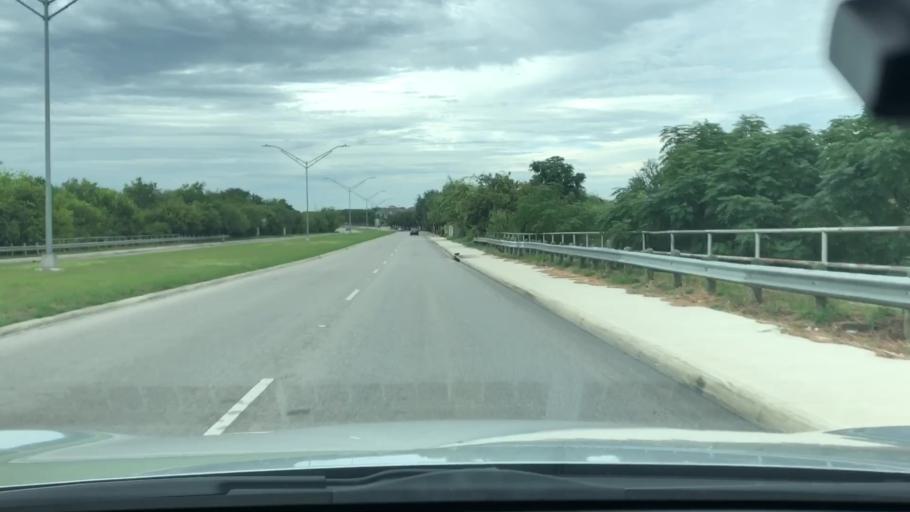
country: US
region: Texas
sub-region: Bexar County
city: Leon Valley
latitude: 29.4494
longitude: -98.6690
